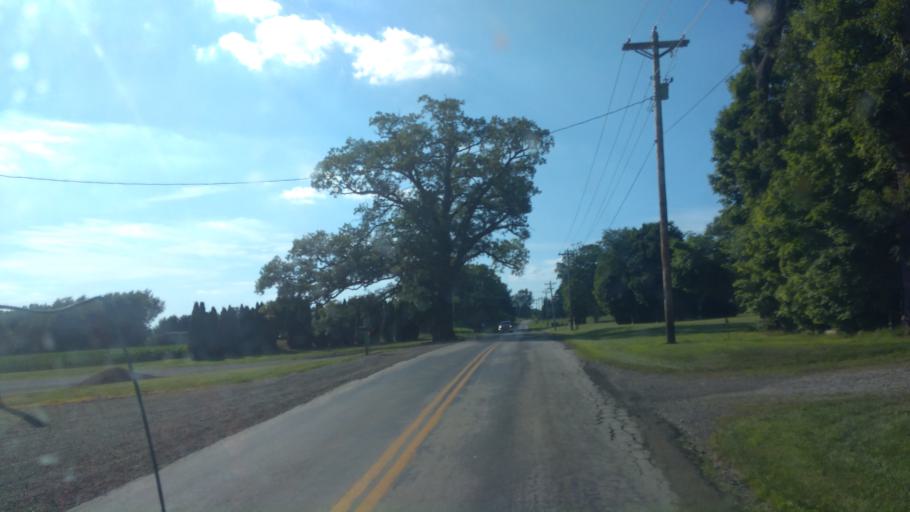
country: US
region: Ohio
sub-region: Wayne County
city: Shreve
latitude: 40.7331
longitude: -82.0601
